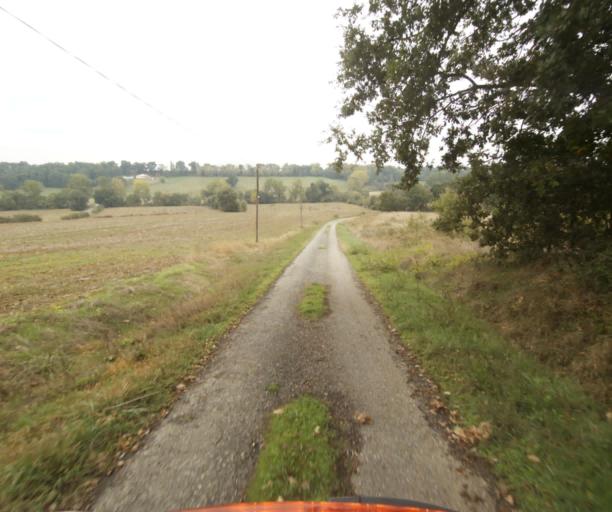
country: FR
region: Midi-Pyrenees
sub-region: Departement de la Haute-Garonne
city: Launac
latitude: 43.7971
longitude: 1.2106
